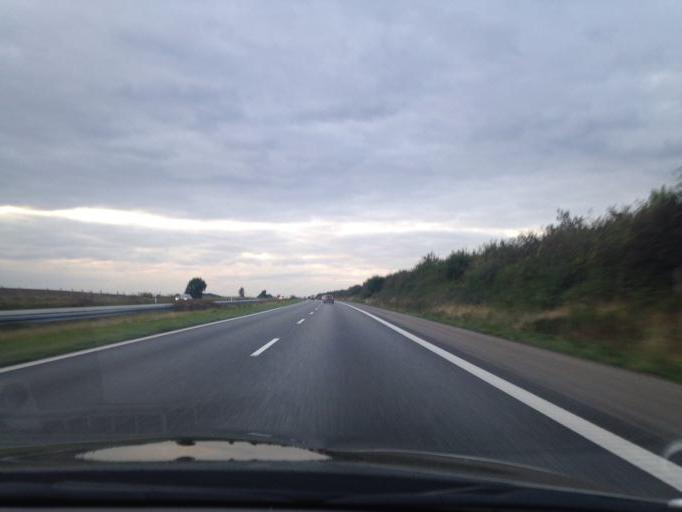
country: DK
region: South Denmark
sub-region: Kolding Kommune
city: Christiansfeld
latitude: 55.3905
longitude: 9.4481
